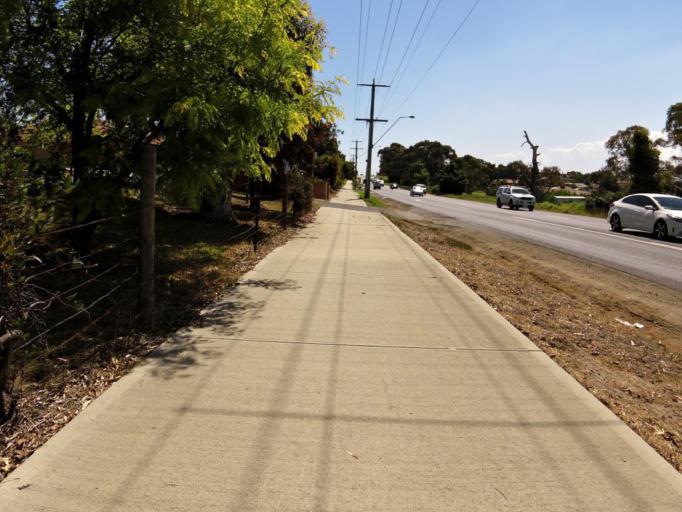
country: AU
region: Victoria
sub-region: Casey
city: Hallam
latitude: -38.0295
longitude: 145.2763
